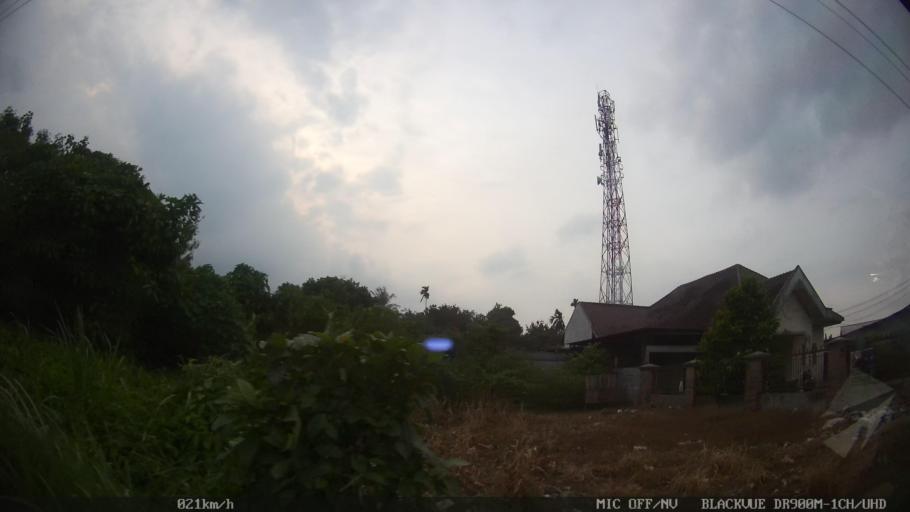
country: ID
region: North Sumatra
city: Sunggal
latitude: 3.5736
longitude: 98.5852
